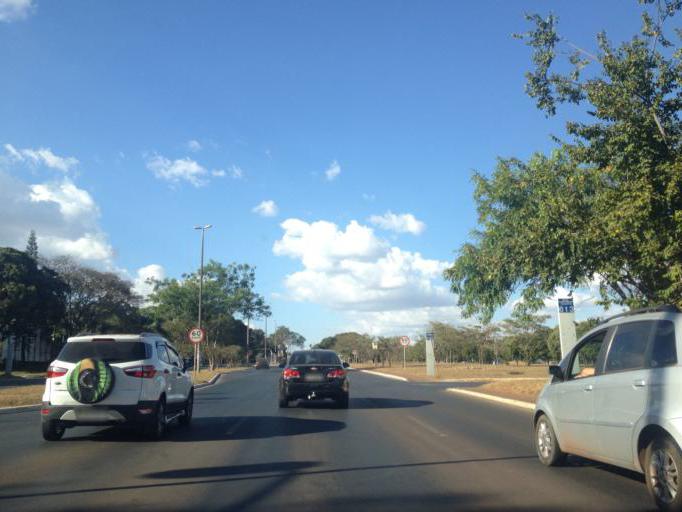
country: BR
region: Federal District
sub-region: Brasilia
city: Brasilia
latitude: -15.8324
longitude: -47.9109
